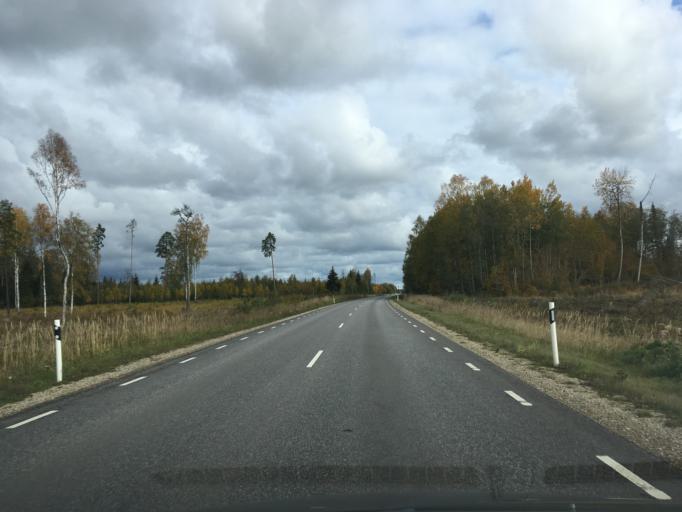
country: EE
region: Harju
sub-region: Anija vald
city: Kehra
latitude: 59.2457
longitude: 25.3029
